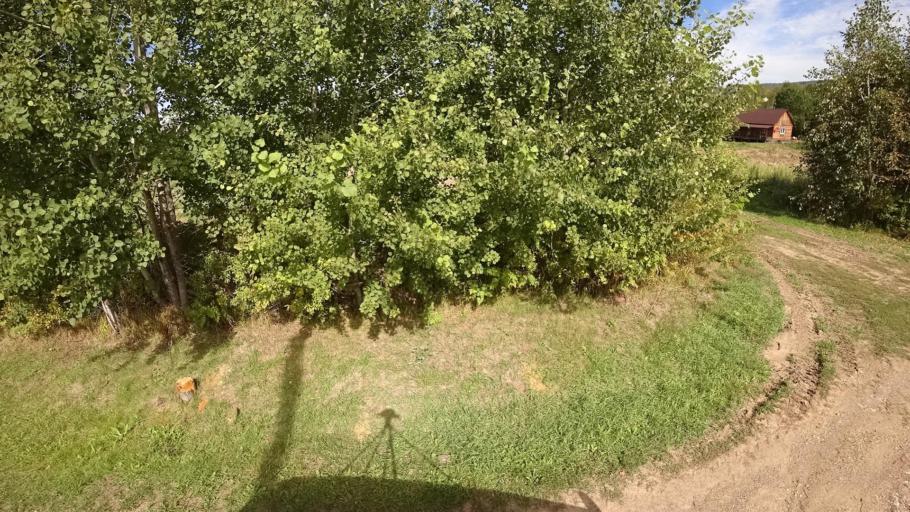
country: RU
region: Primorskiy
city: Yakovlevka
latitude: 44.3954
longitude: 133.6013
